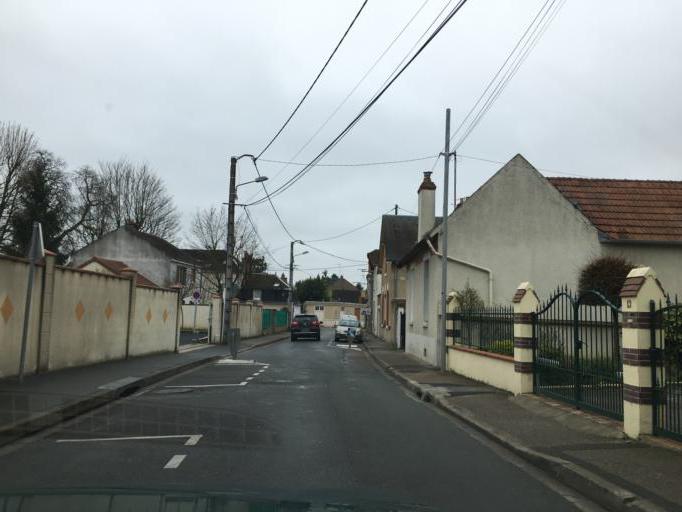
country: FR
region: Centre
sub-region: Departement du Loiret
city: Saint-Jean-le-Blanc
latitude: 47.9093
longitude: 1.9298
